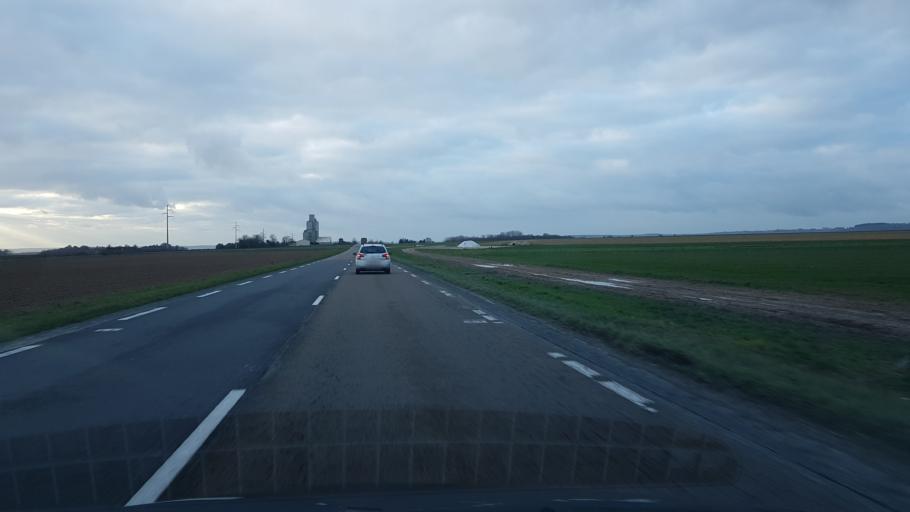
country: FR
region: Champagne-Ardenne
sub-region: Departement de la Marne
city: Connantre
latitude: 48.7277
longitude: 3.8669
